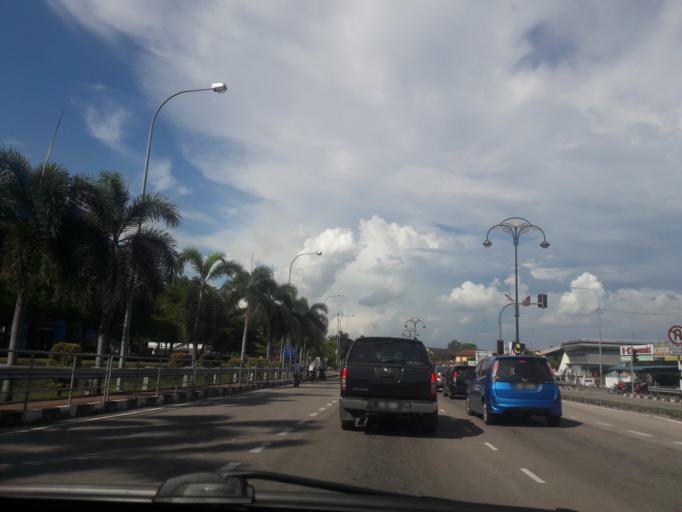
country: MY
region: Kedah
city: Sungai Petani
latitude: 5.6223
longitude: 100.4766
